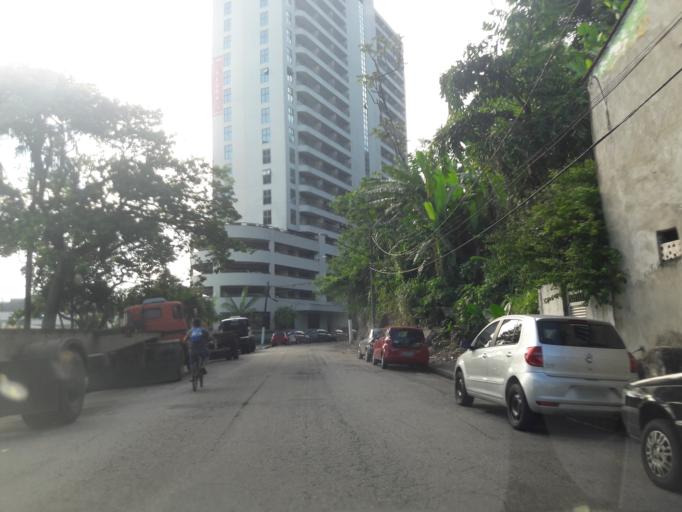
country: BR
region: Sao Paulo
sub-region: Santos
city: Santos
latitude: -23.9316
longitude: -46.3388
